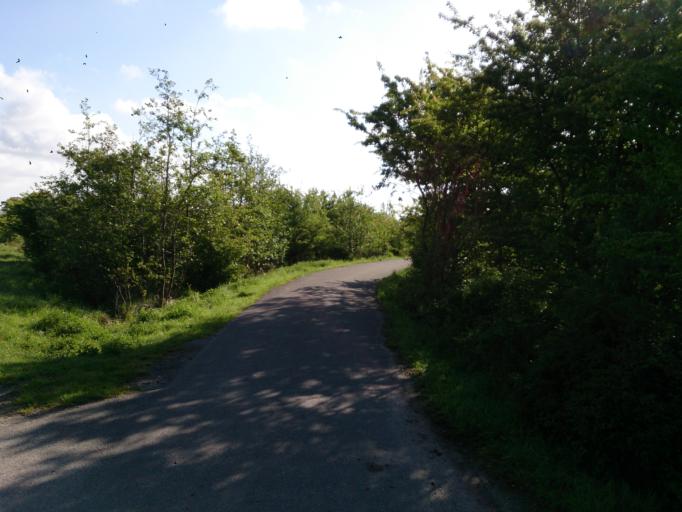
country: DK
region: Capital Region
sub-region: Tarnby Kommune
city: Tarnby
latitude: 55.6159
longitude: 12.5763
